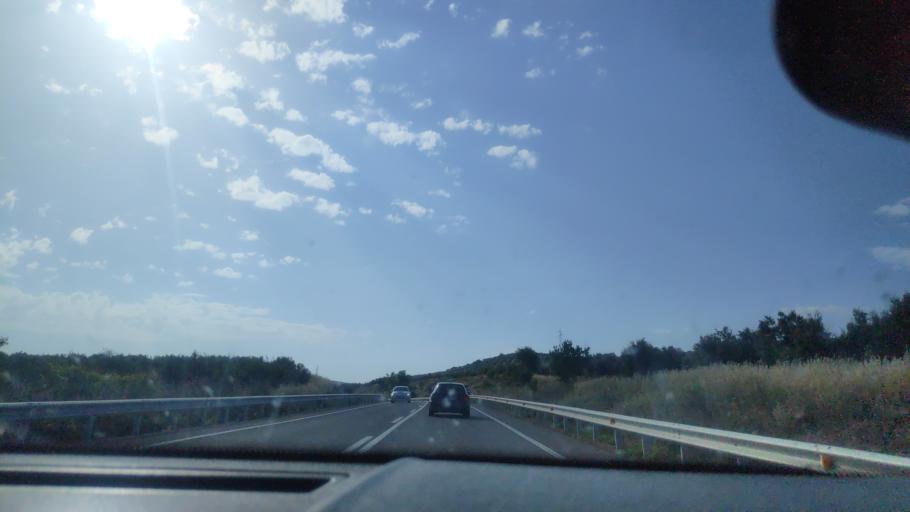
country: ES
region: Andalusia
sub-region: Provincia de Jaen
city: Frailes
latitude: 37.4399
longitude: -3.8207
